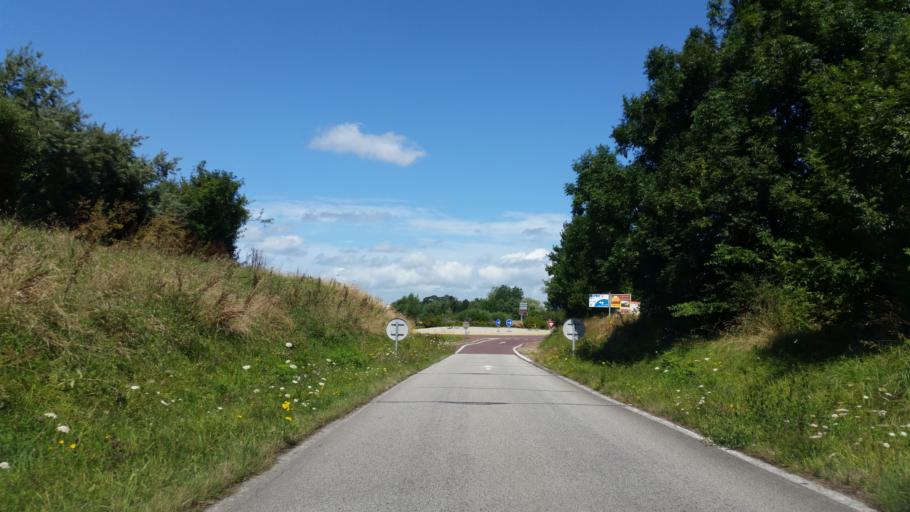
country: FR
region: Lower Normandy
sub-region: Departement de la Manche
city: Sainte-Mere-Eglise
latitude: 49.4021
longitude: -1.3099
